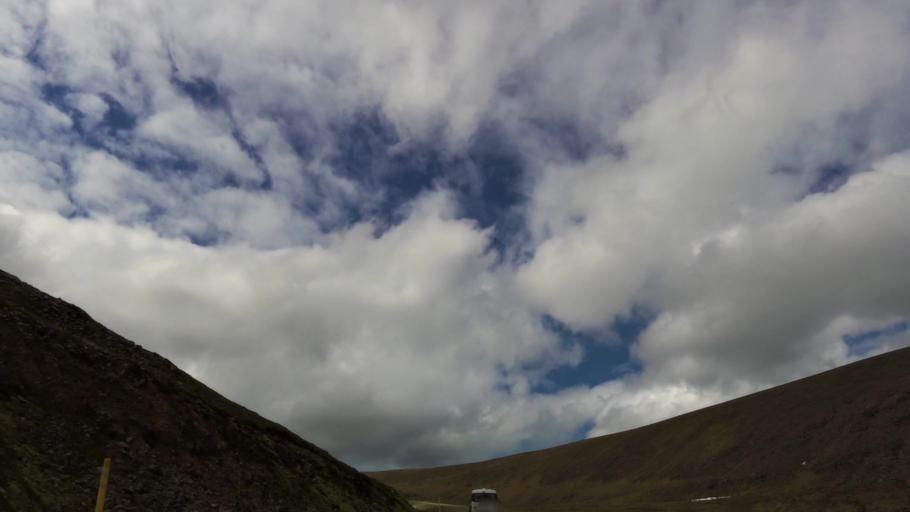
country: IS
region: Westfjords
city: Isafjoerdur
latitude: 66.1688
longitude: -23.3471
